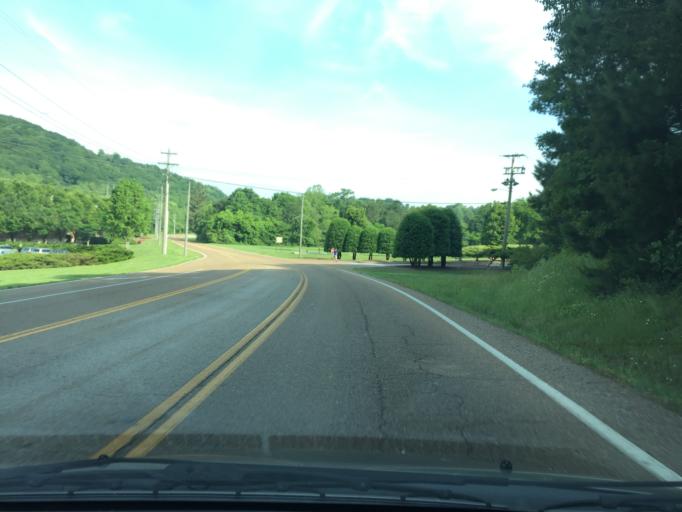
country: US
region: Tennessee
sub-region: Hamilton County
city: Apison
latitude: 35.0422
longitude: -85.0306
